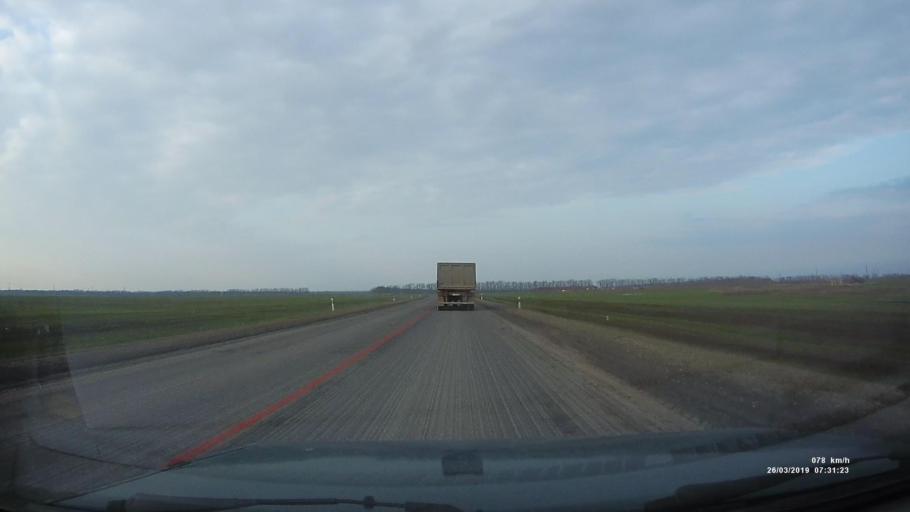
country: RU
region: Rostov
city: Novobessergenovka
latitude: 47.2333
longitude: 38.7920
